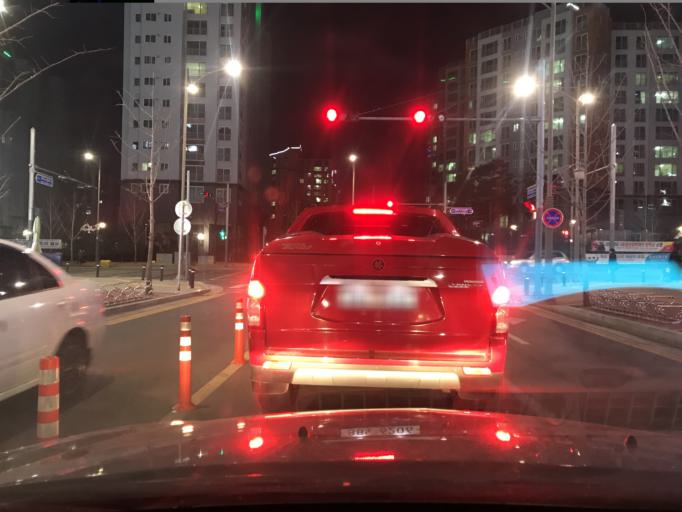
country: KR
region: Daegu
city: Hwawon
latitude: 35.6924
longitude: 128.4547
